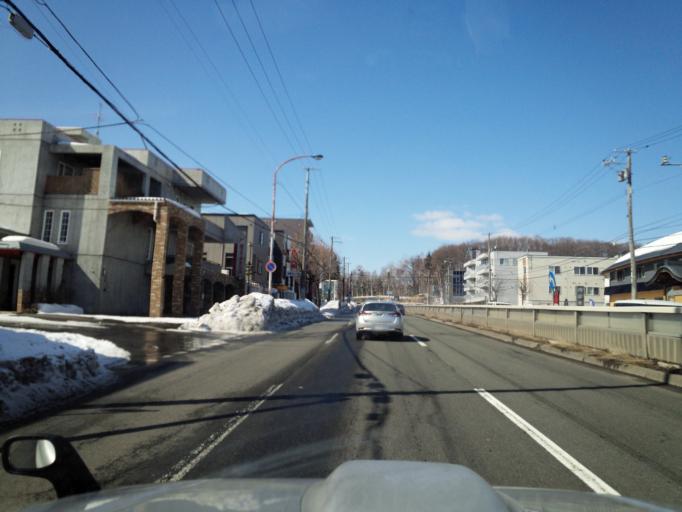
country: JP
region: Hokkaido
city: Sapporo
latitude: 43.0034
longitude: 141.4278
